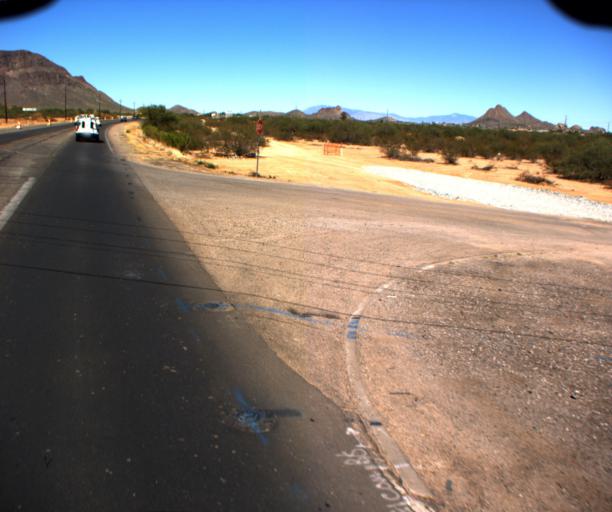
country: US
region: Arizona
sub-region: Pima County
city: Tucson Estates
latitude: 32.1640
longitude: -111.0971
